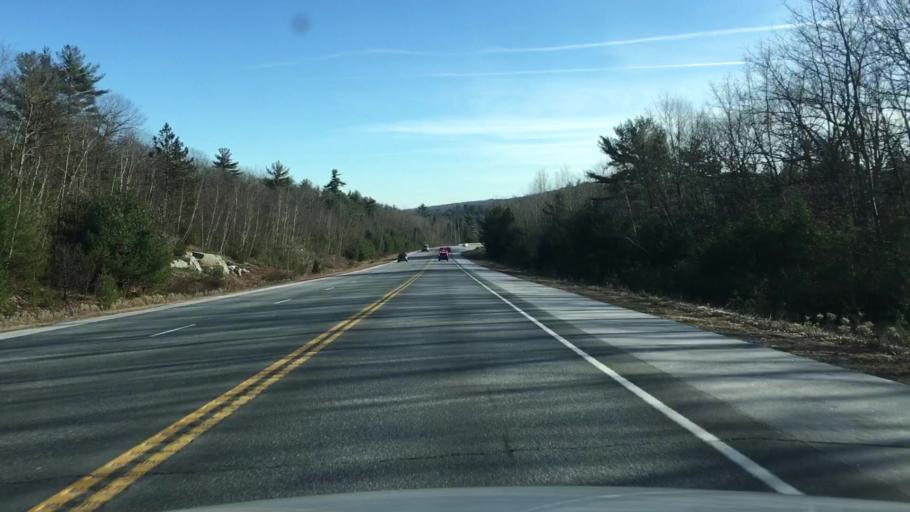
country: US
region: Maine
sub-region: Hancock County
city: Dedham
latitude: 44.6851
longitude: -68.5812
